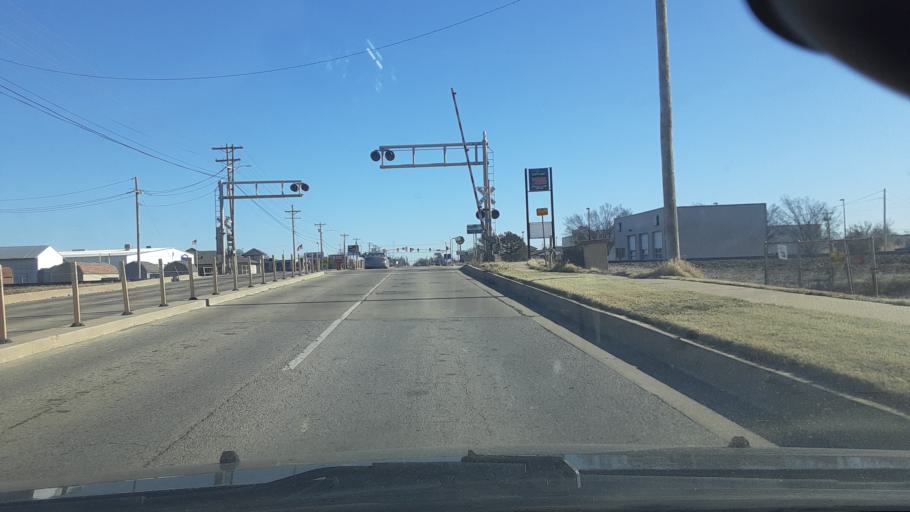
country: US
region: Oklahoma
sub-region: Kay County
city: Ponca City
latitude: 36.7386
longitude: -97.0776
